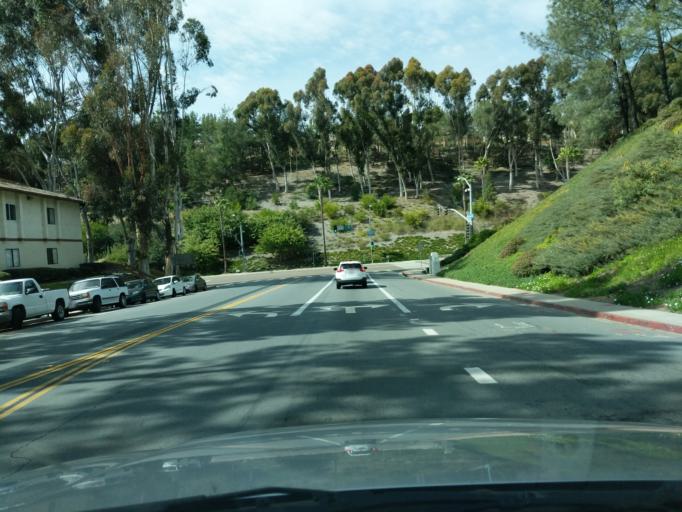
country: US
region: California
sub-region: San Diego County
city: La Mesa
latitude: 32.7887
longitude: -117.1086
